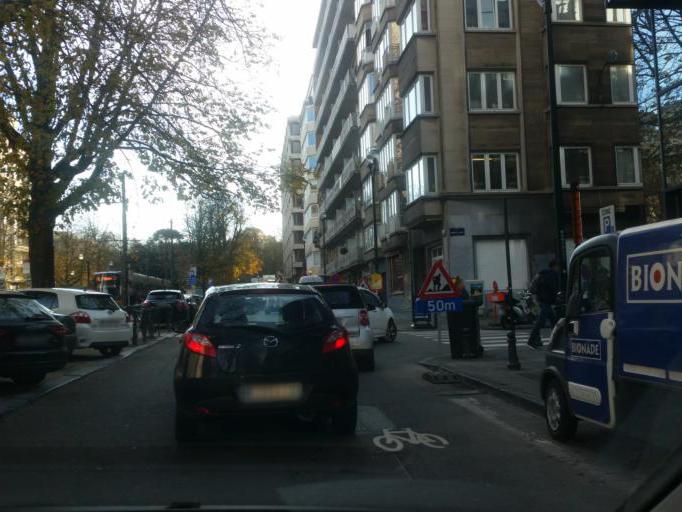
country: BE
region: Brussels Capital
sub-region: Bruxelles-Capitale
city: Brussels
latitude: 50.8166
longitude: 4.3716
